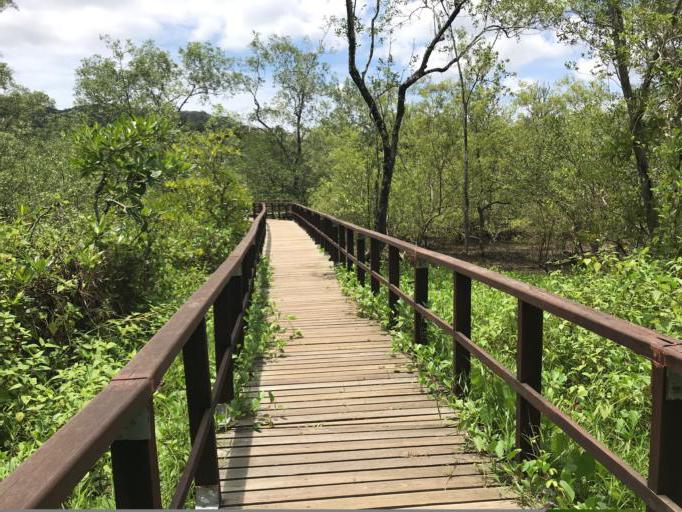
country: MY
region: Sarawak
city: Kuching
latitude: 1.7207
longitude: 110.4473
